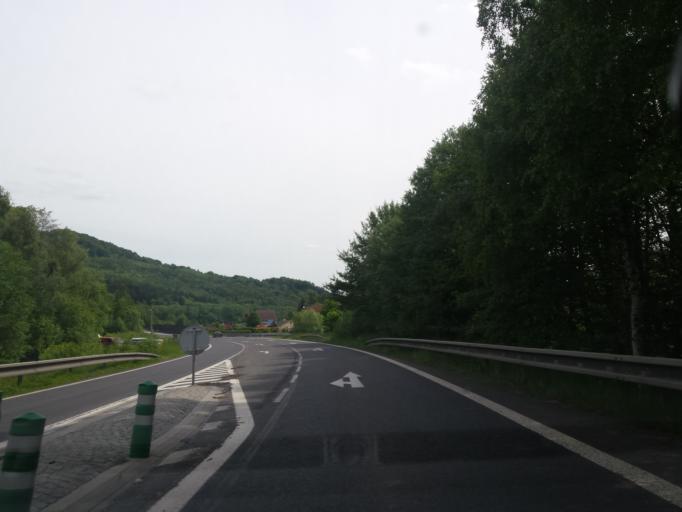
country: CZ
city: Novy Bor
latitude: 50.7565
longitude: 14.5338
